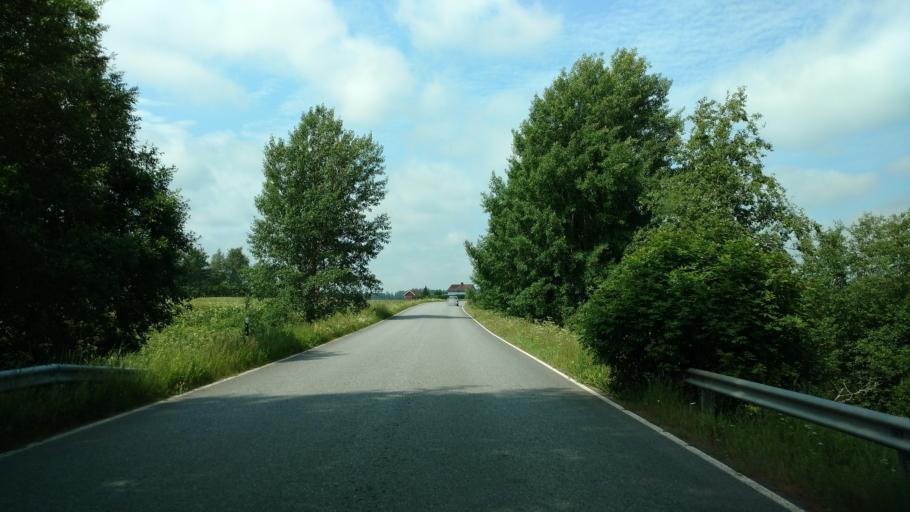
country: FI
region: Haeme
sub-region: Forssa
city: Ypaejae
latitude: 60.8005
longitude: 23.3426
